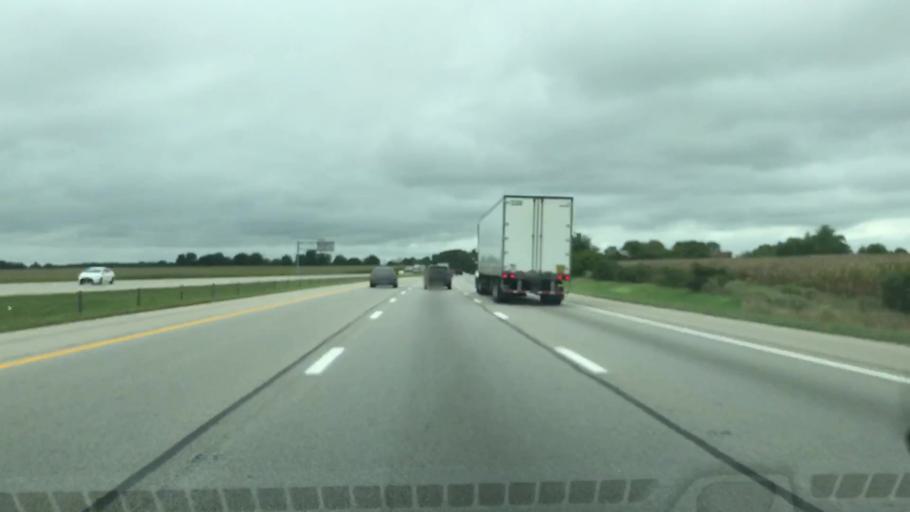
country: US
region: Ohio
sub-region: Clark County
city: Lisbon
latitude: 39.9340
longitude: -83.6730
